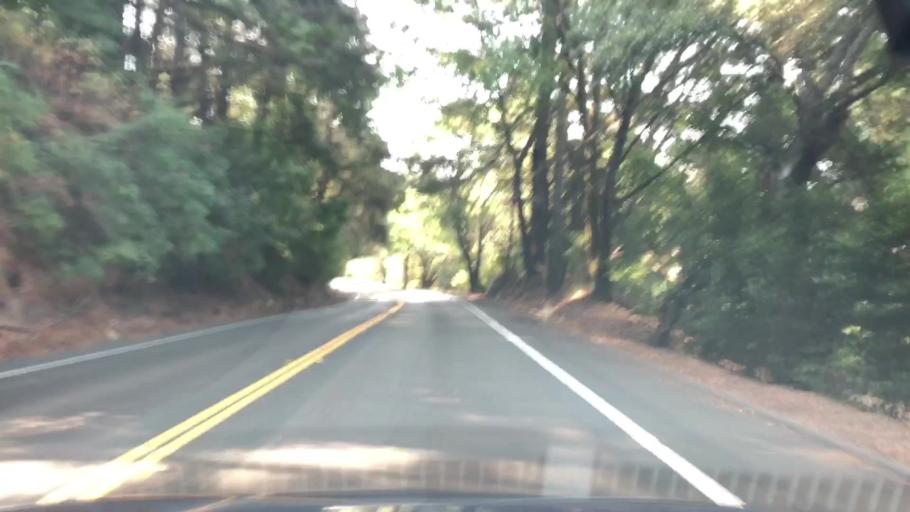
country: US
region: California
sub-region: Napa County
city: Calistoga
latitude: 38.5685
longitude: -122.6268
